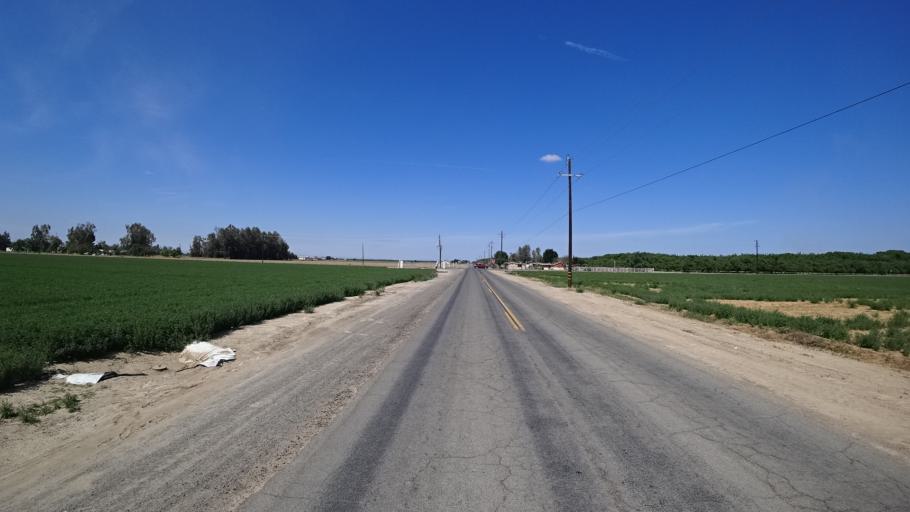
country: US
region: California
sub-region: Kings County
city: Home Garden
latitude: 36.2693
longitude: -119.6715
